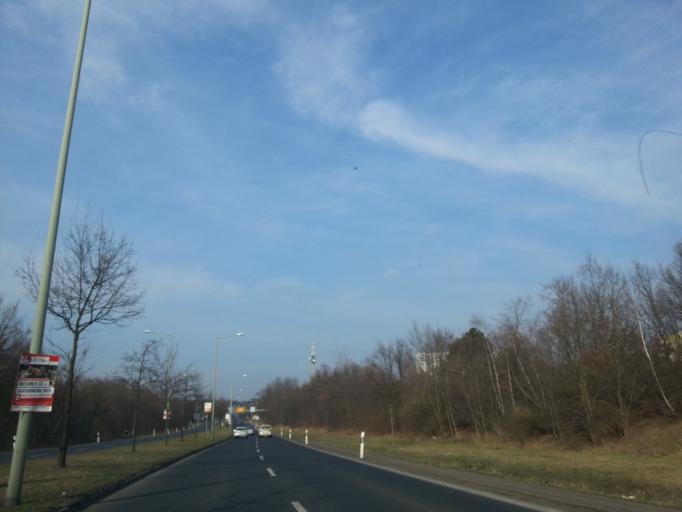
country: DE
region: Saxony
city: Albertstadt
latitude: 51.0964
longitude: 13.7364
